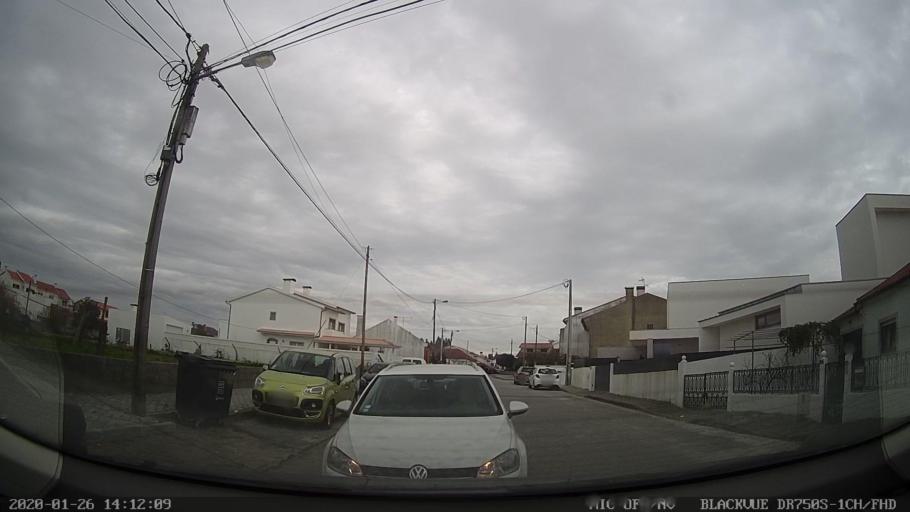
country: PT
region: Aveiro
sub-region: Aveiro
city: Aradas
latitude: 40.6275
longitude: -8.6260
